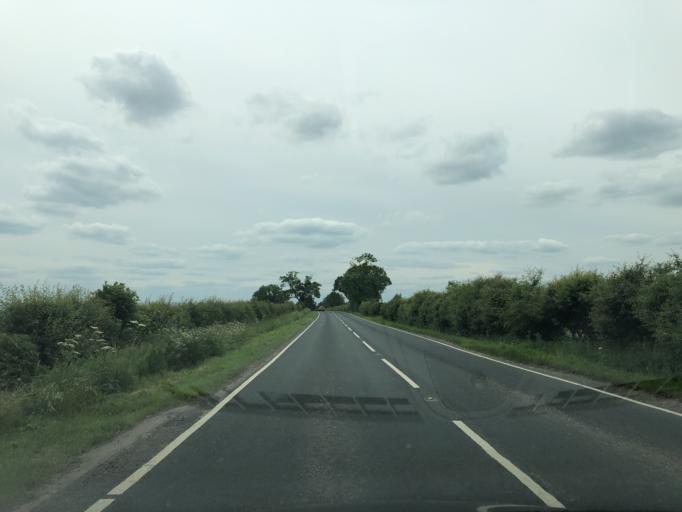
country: GB
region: England
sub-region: North Yorkshire
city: Thirsk
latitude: 54.2325
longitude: -1.3021
